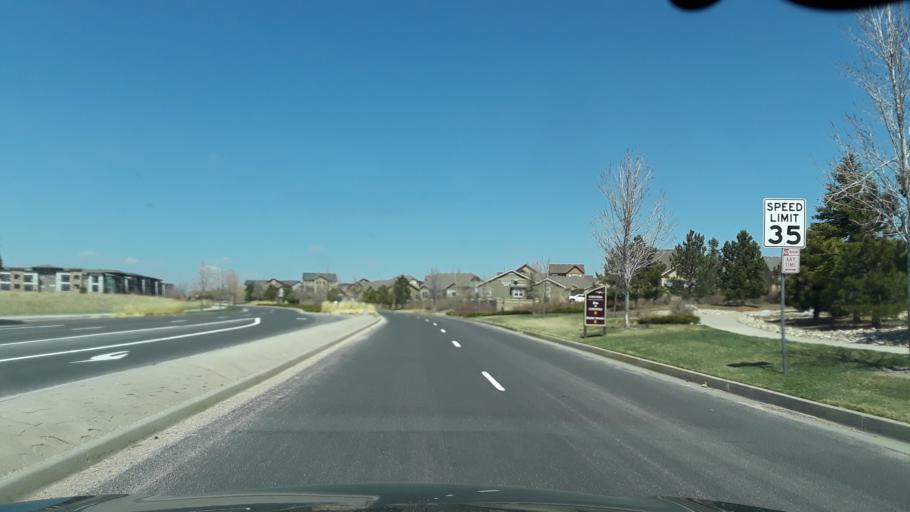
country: US
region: Colorado
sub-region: El Paso County
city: Black Forest
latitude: 38.9716
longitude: -104.7386
